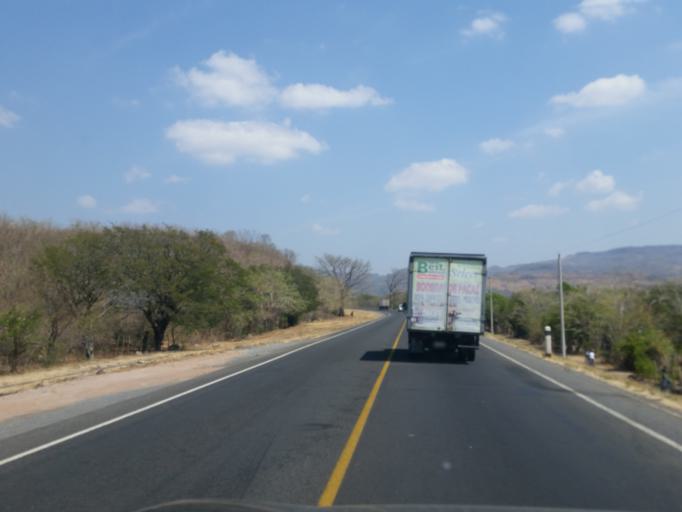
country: NI
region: Boaco
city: Teustepe
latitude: 12.4694
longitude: -86.0394
